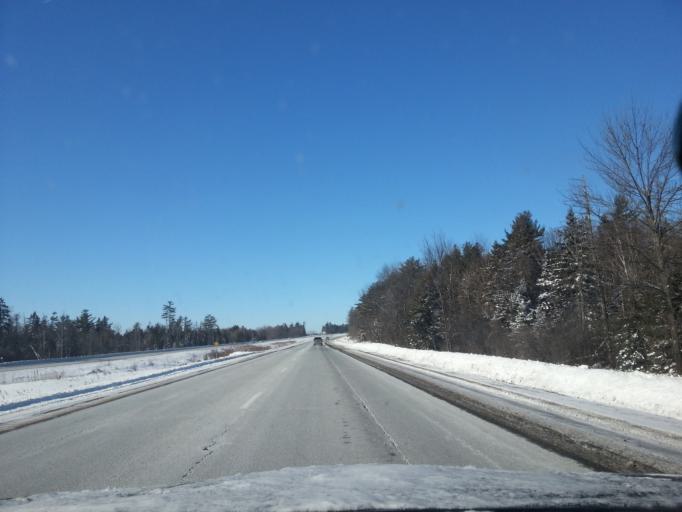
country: CA
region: Ontario
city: Carleton Place
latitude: 45.3347
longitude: -76.1714
